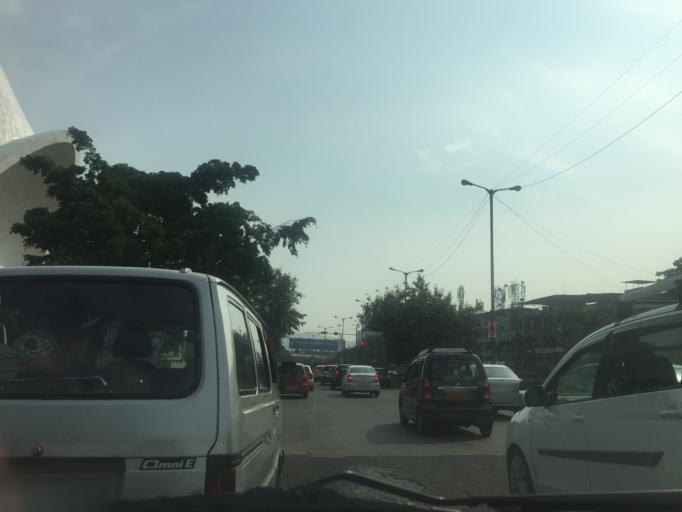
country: IN
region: Maharashtra
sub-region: Thane
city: Airoli
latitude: 19.1493
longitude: 72.9892
